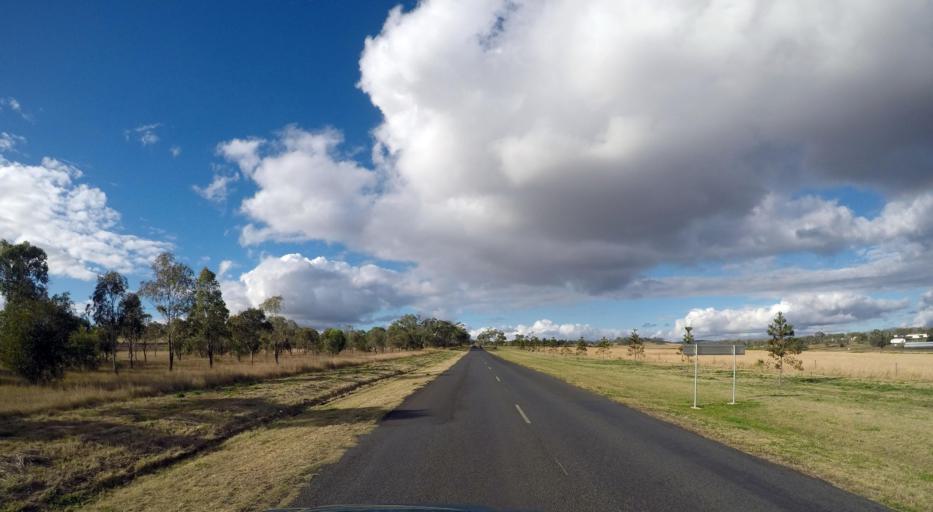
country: AU
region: Queensland
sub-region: Toowoomba
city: Westbrook
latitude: -27.7068
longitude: 151.6500
